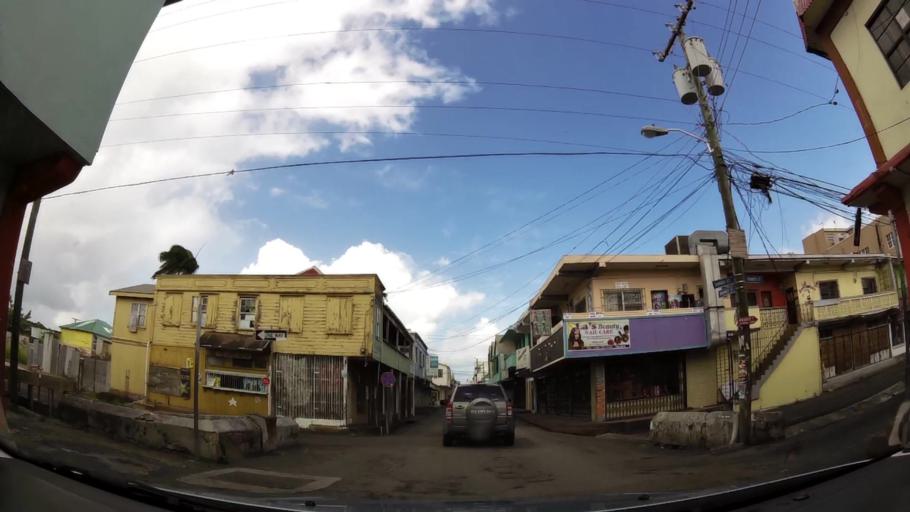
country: AG
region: Saint John
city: Saint John's
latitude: 17.1192
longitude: -61.8439
